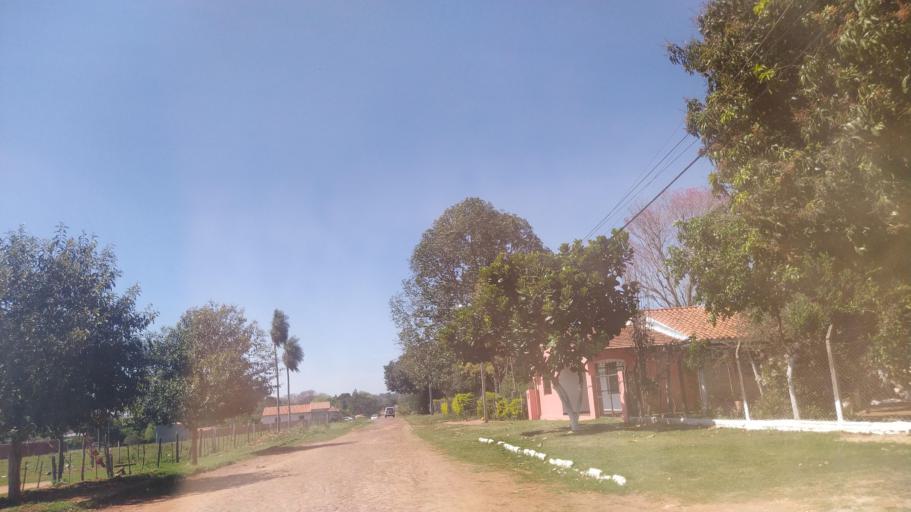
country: PY
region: Misiones
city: San Juan Bautista
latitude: -26.6618
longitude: -57.1534
